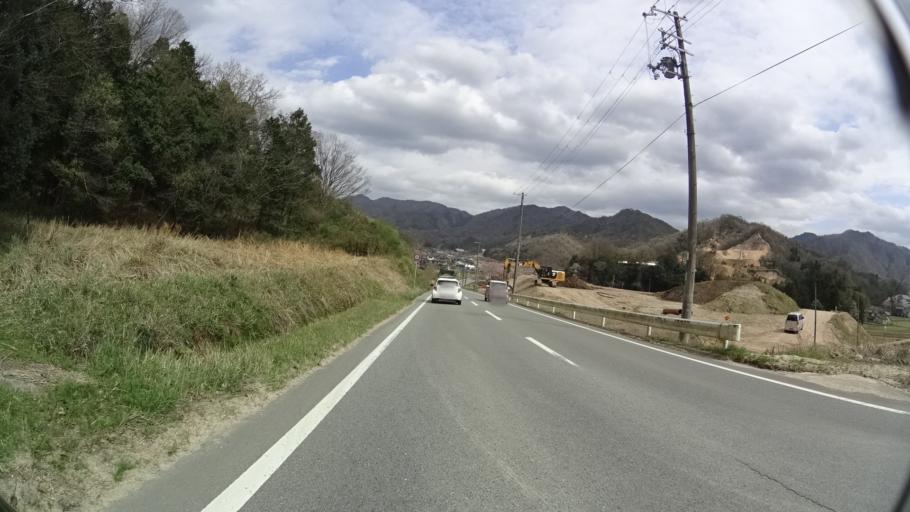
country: JP
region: Hyogo
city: Toyooka
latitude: 35.5024
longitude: 134.8728
